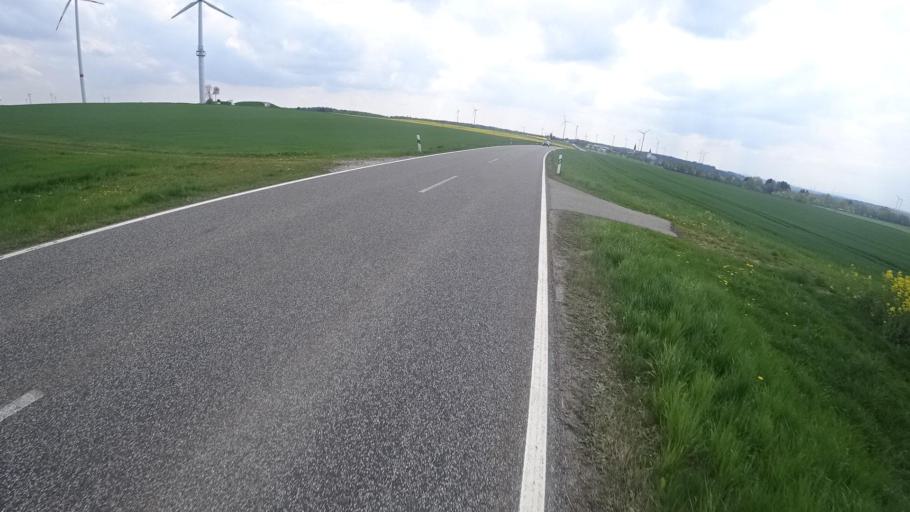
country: DE
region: Rheinland-Pfalz
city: Laubach
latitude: 50.0630
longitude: 7.5136
